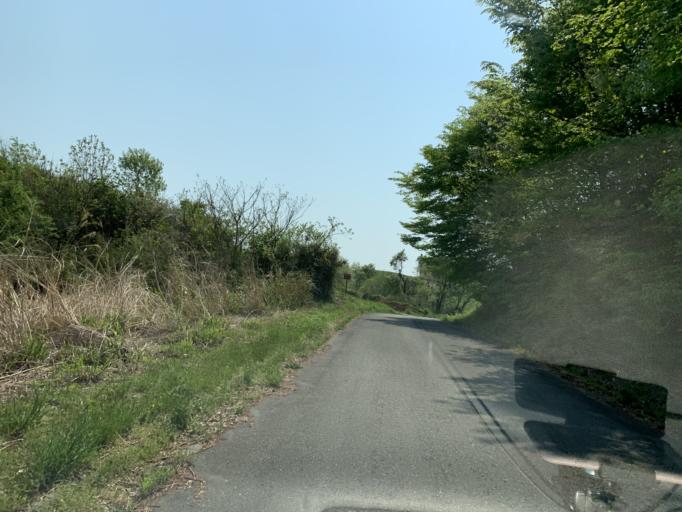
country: JP
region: Iwate
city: Ichinoseki
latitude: 38.8829
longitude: 141.0593
